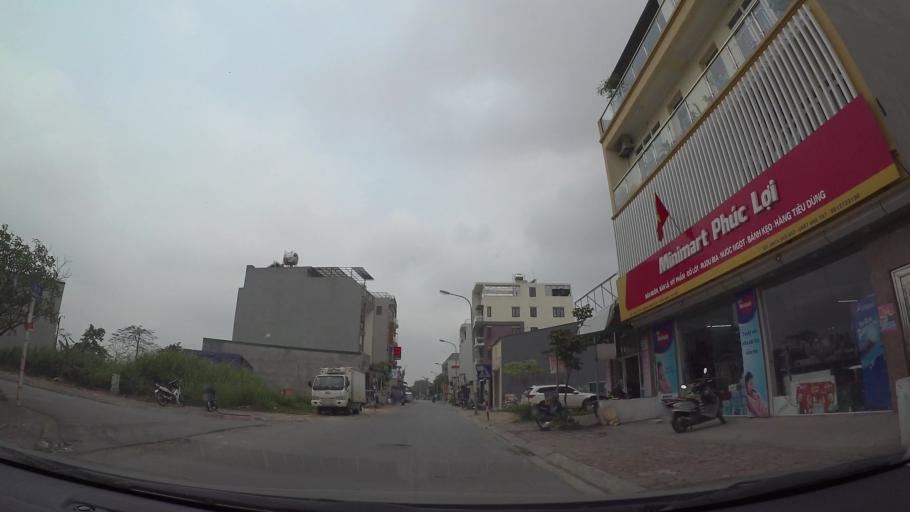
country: VN
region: Ha Noi
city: Trau Quy
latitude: 21.0386
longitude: 105.9306
